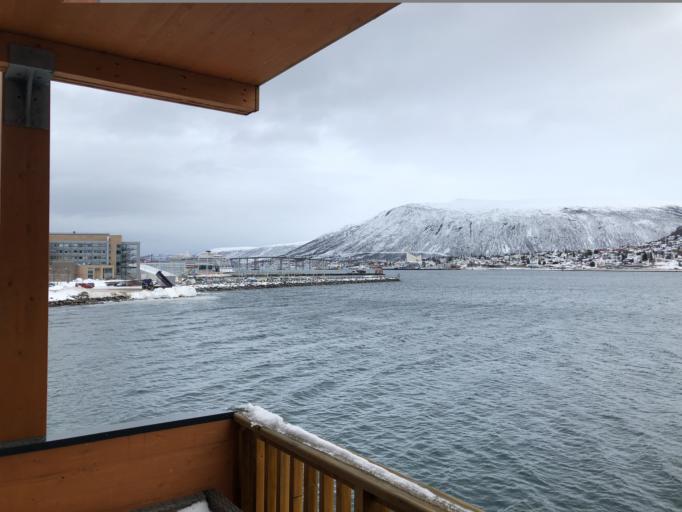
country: NO
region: Troms
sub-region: Tromso
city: Tromso
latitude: 69.6407
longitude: 18.9442
